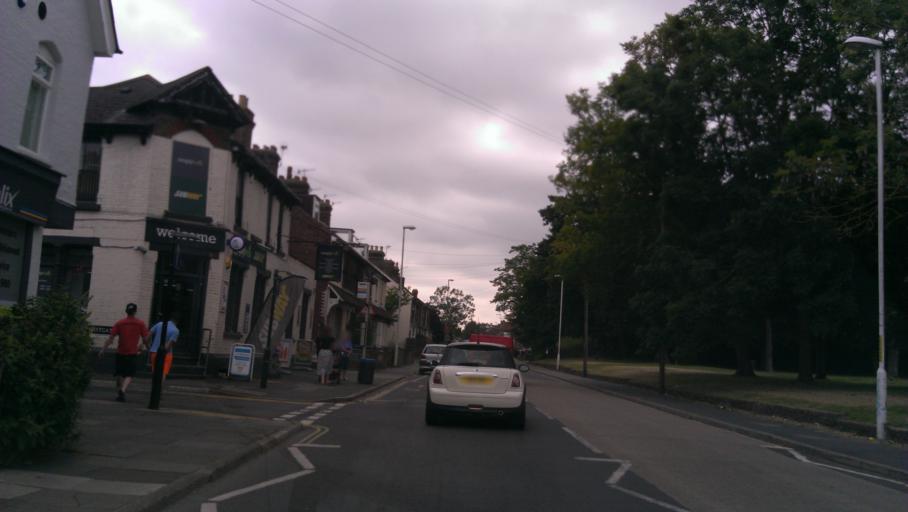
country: GB
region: England
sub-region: Kent
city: Faversham
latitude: 51.3141
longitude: 0.8977
